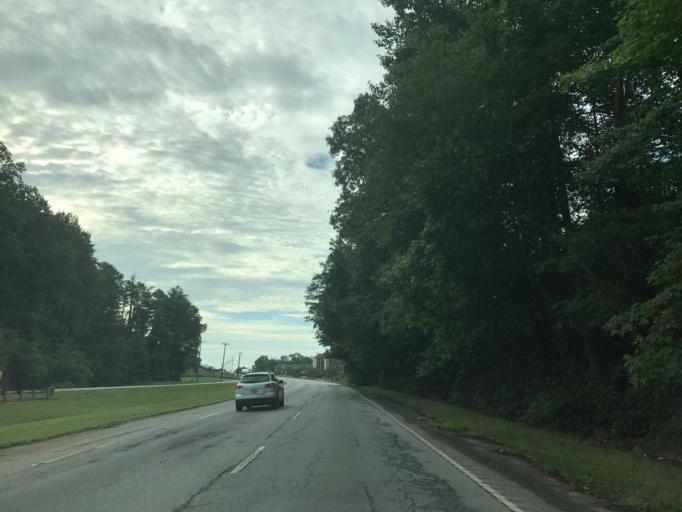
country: US
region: South Carolina
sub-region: Greenville County
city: Mauldin
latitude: 34.8060
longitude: -82.3275
